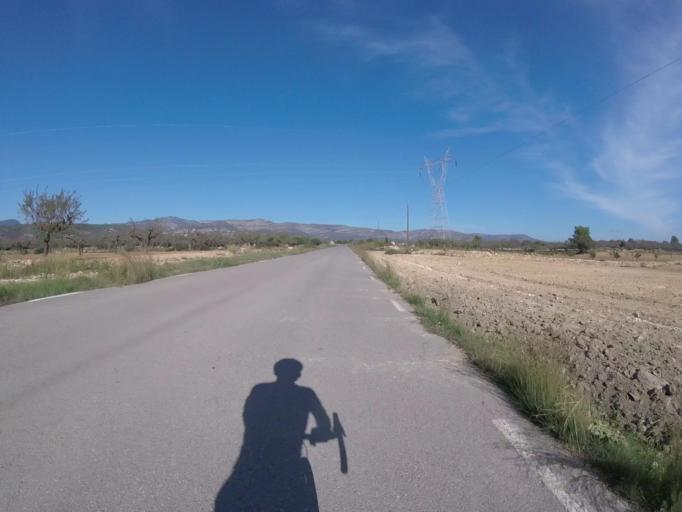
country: ES
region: Valencia
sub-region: Provincia de Castello
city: Sarratella
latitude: 40.2657
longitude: 0.0658
